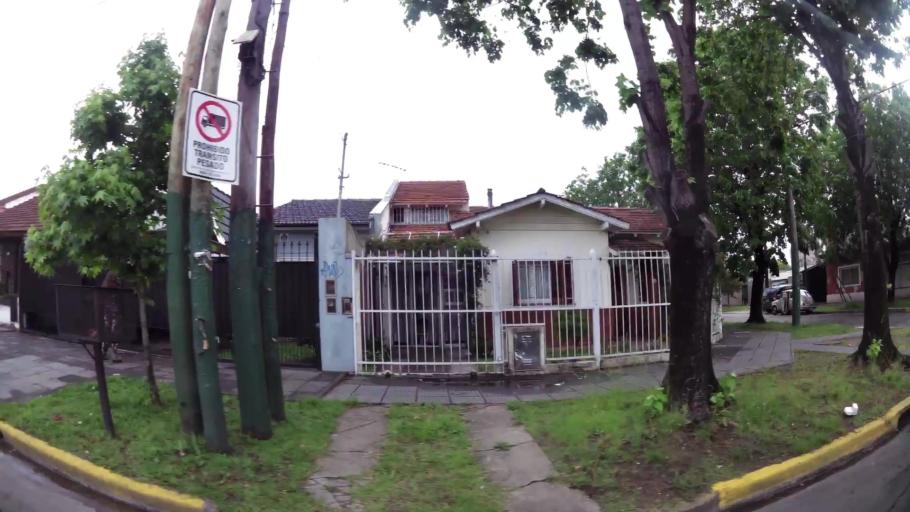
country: AR
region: Buenos Aires
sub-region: Partido de Lomas de Zamora
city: Lomas de Zamora
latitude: -34.7588
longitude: -58.3815
